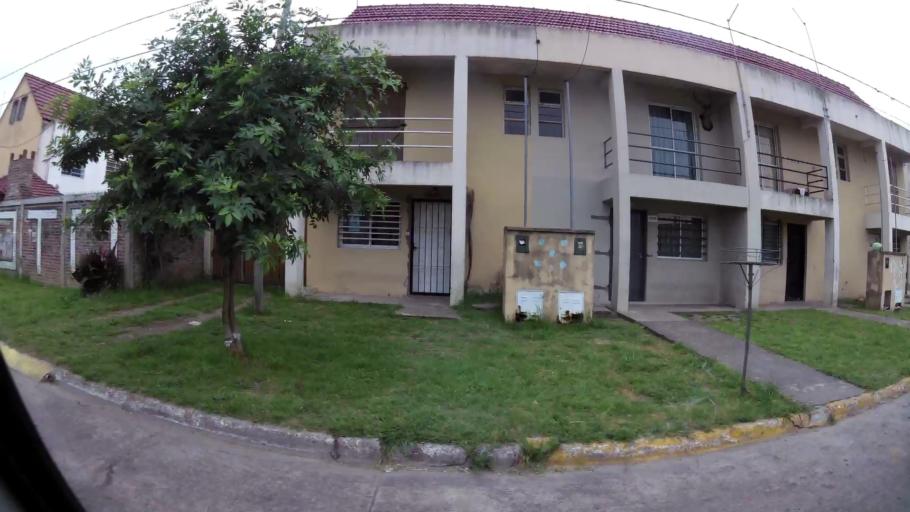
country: AR
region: Buenos Aires
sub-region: Partido de La Plata
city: La Plata
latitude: -34.9042
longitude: -57.9884
